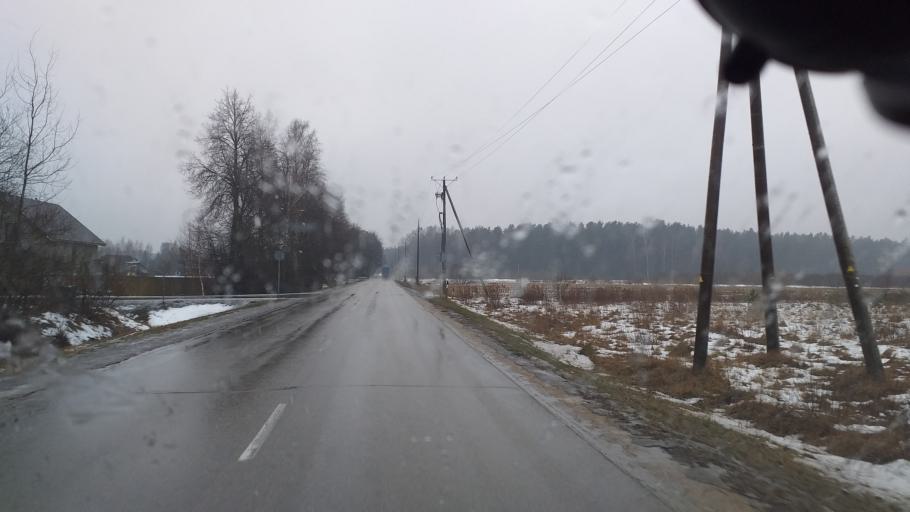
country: LV
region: Babite
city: Pinki
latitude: 56.9677
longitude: 23.9671
